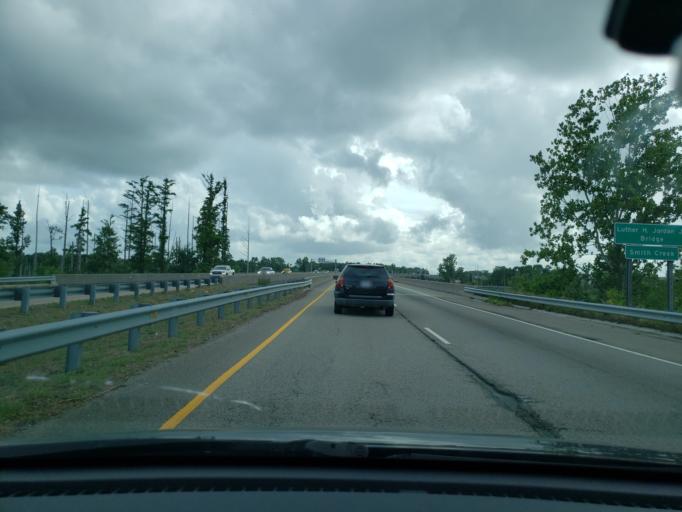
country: US
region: North Carolina
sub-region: New Hanover County
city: Wrightsboro
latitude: 34.2595
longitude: -77.9346
